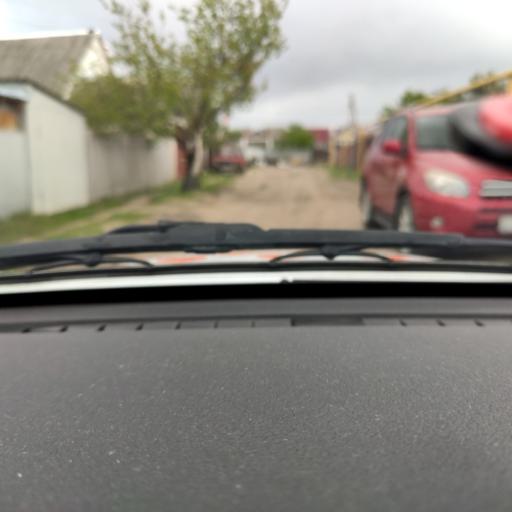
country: RU
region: Voronezj
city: Podgornoye
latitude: 51.7422
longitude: 39.1560
